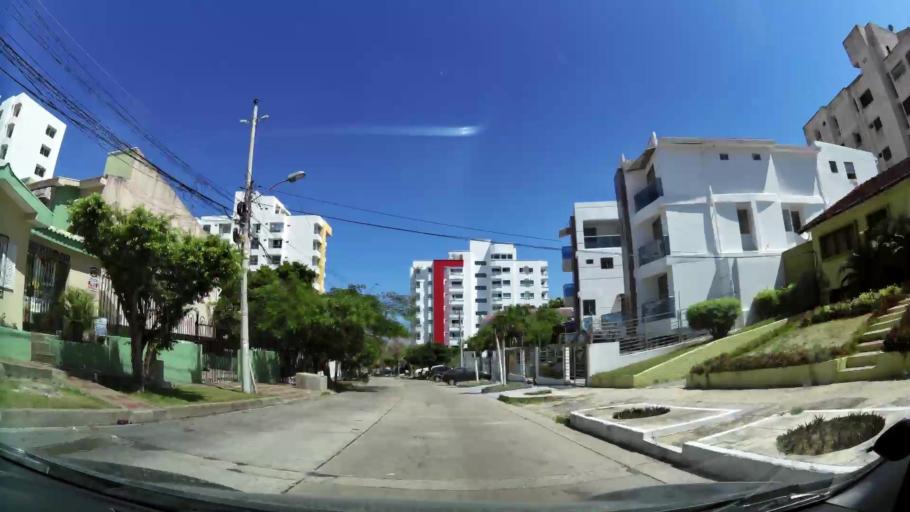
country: CO
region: Atlantico
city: Barranquilla
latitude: 10.9912
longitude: -74.8173
